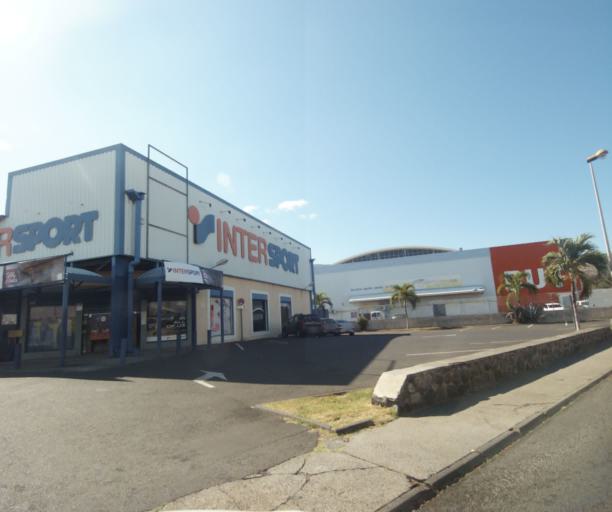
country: RE
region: Reunion
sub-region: Reunion
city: Saint-Paul
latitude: -20.9864
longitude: 55.2920
